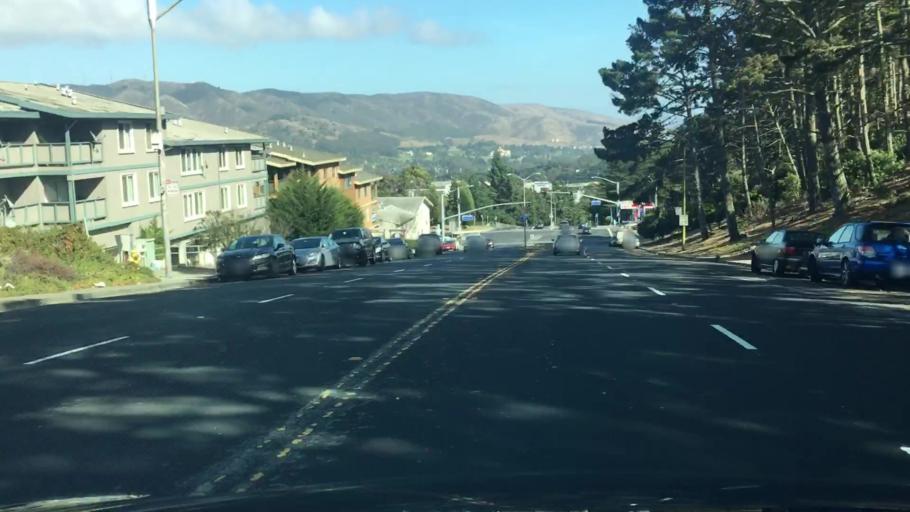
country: US
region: California
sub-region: San Mateo County
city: Broadmoor
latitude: 37.6693
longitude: -122.4775
